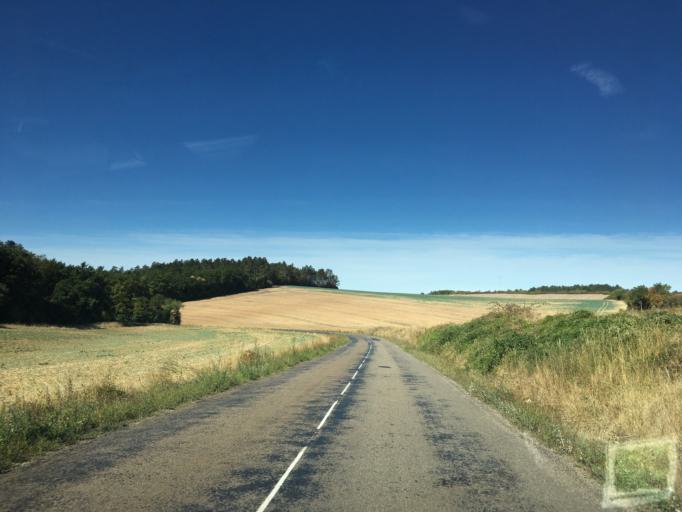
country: FR
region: Bourgogne
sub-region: Departement de l'Yonne
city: Vermenton
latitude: 47.5917
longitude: 3.6973
